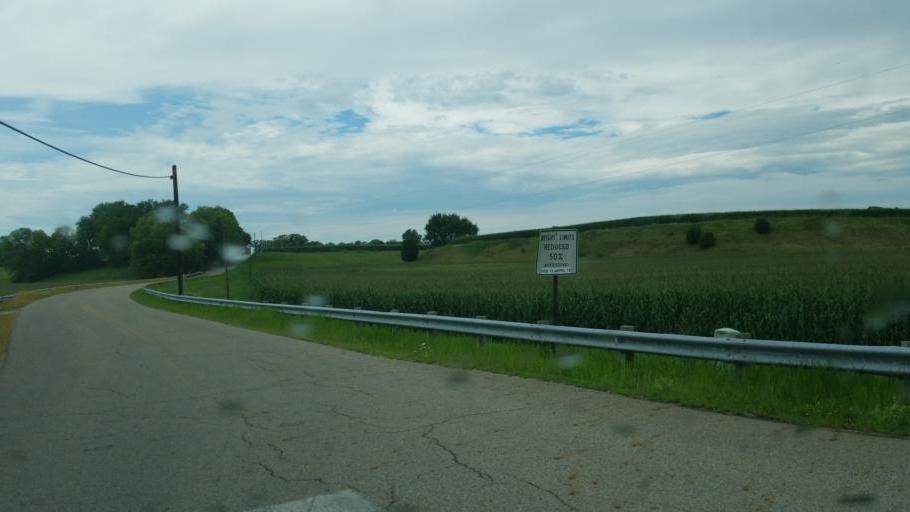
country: US
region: Ohio
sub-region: Pickaway County
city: Ashville
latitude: 39.7053
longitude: -82.9218
